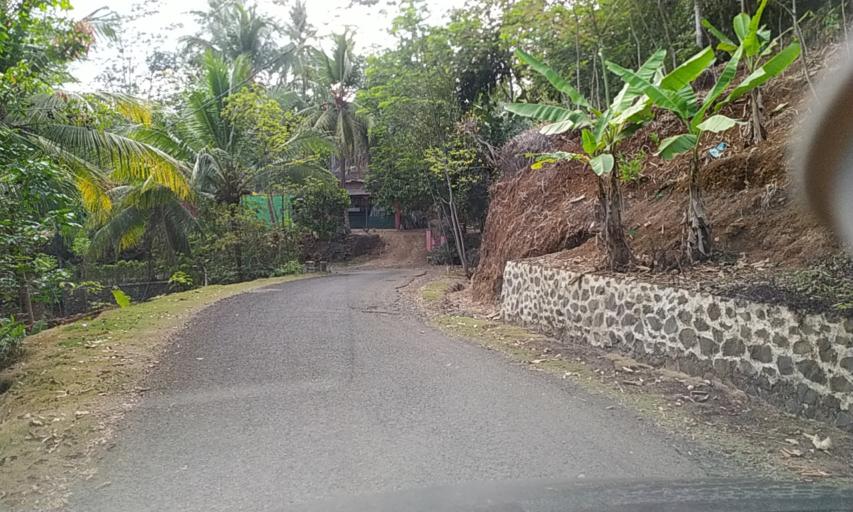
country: ID
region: Central Java
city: Pasirmanggu
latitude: -7.2272
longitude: 108.5935
